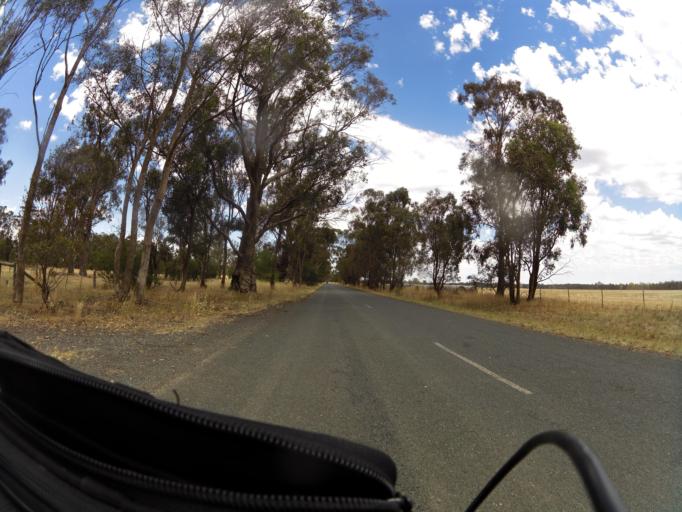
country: AU
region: Victoria
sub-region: Greater Shepparton
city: Shepparton
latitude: -36.6609
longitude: 145.1997
